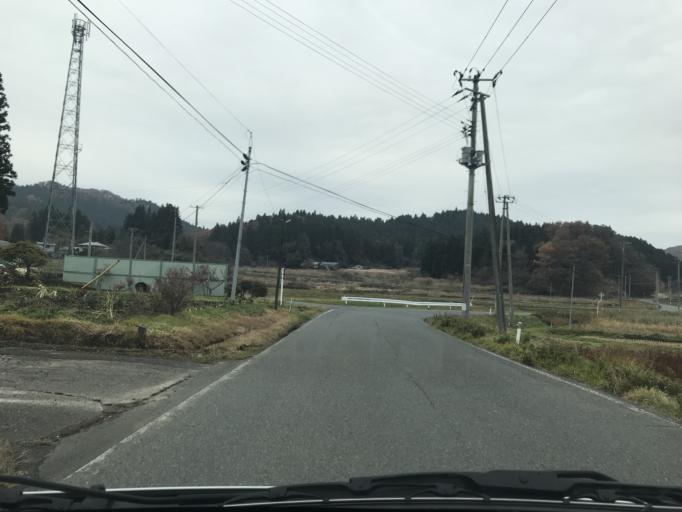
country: JP
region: Iwate
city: Kitakami
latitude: 39.2780
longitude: 141.1736
